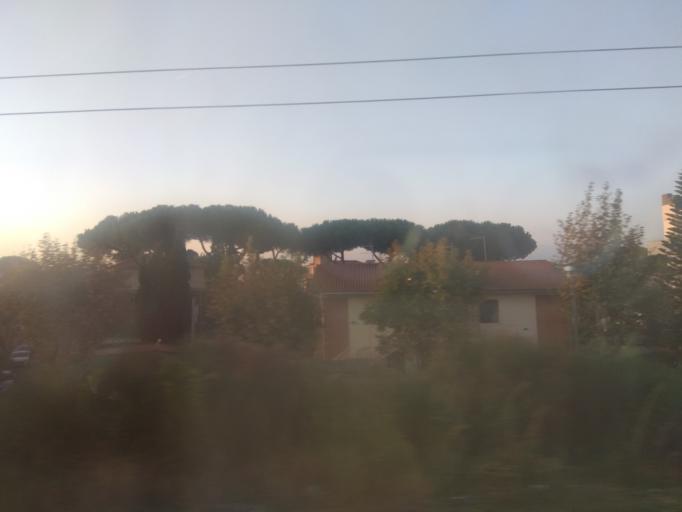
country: IT
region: Latium
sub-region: Citta metropolitana di Roma Capitale
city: Santa Marinella
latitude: 42.0345
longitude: 11.8483
